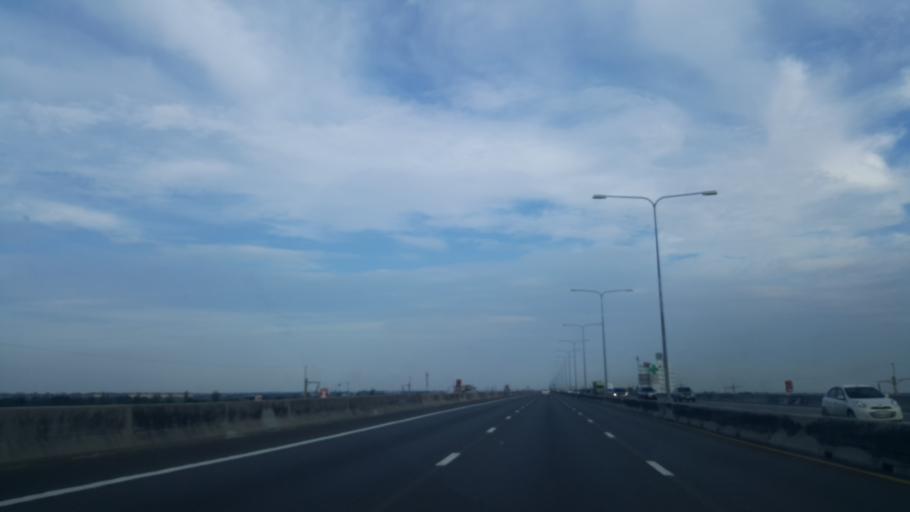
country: TH
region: Samut Prakan
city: Bang Bo
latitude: 13.5853
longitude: 100.8492
